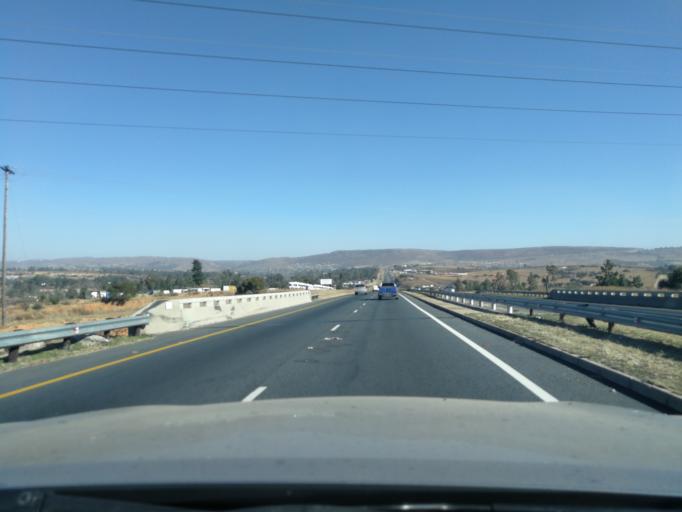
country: ZA
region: Gauteng
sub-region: West Rand District Municipality
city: Muldersdriseloop
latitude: -26.0294
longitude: 27.8493
